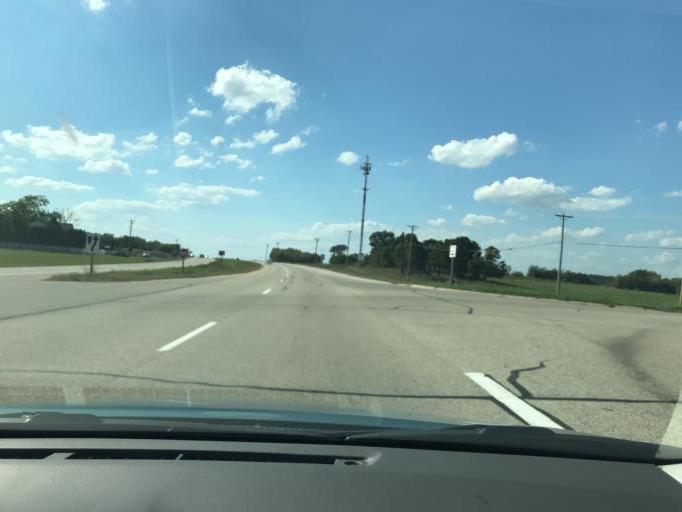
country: US
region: Wisconsin
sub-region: Walworth County
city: Pell Lake
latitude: 42.5963
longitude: -88.3544
